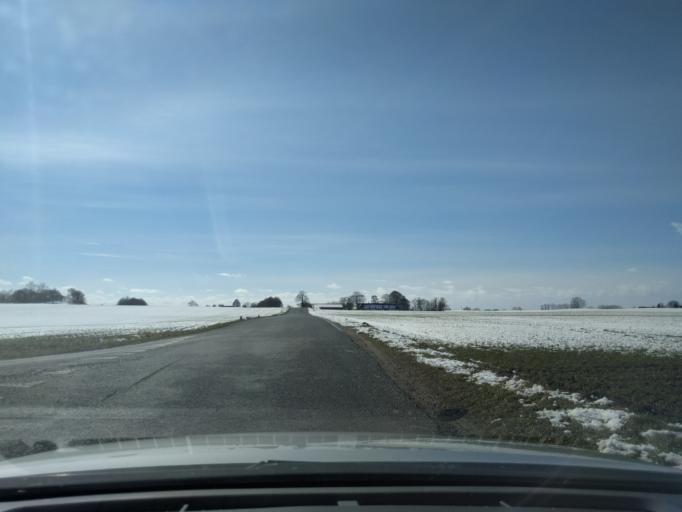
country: DK
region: South Denmark
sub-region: Nyborg Kommune
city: Ullerslev
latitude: 55.3604
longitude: 10.7150
